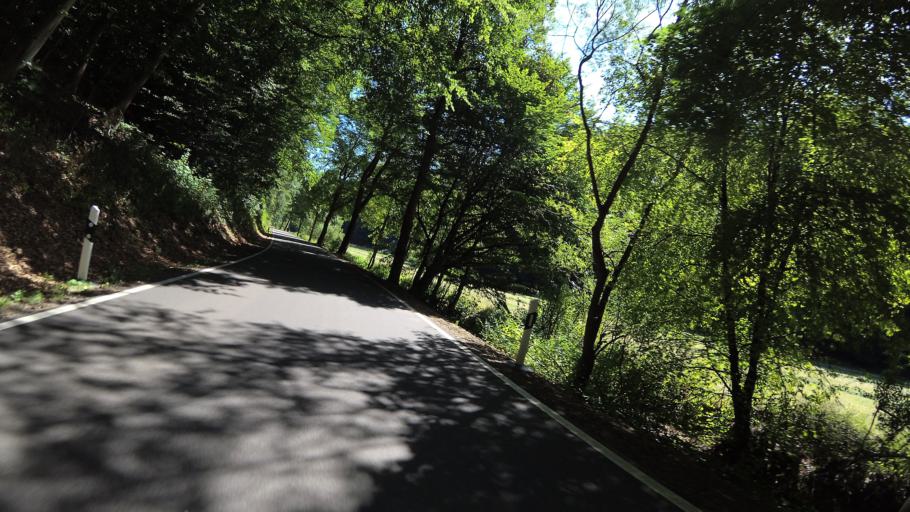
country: DE
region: Rheinland-Pfalz
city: Zweibrucken
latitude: 49.2523
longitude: 7.3123
